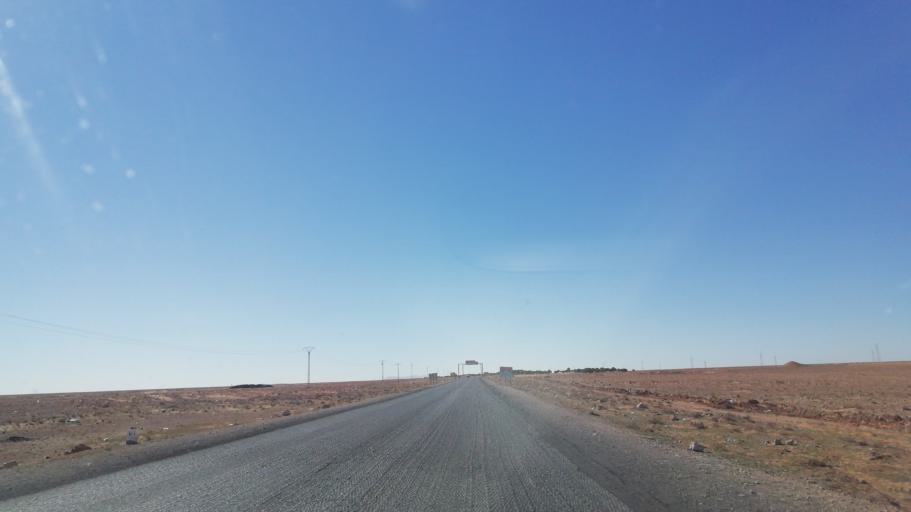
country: DZ
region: Saida
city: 'Ain el Hadjar
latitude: 34.0094
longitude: 0.0521
